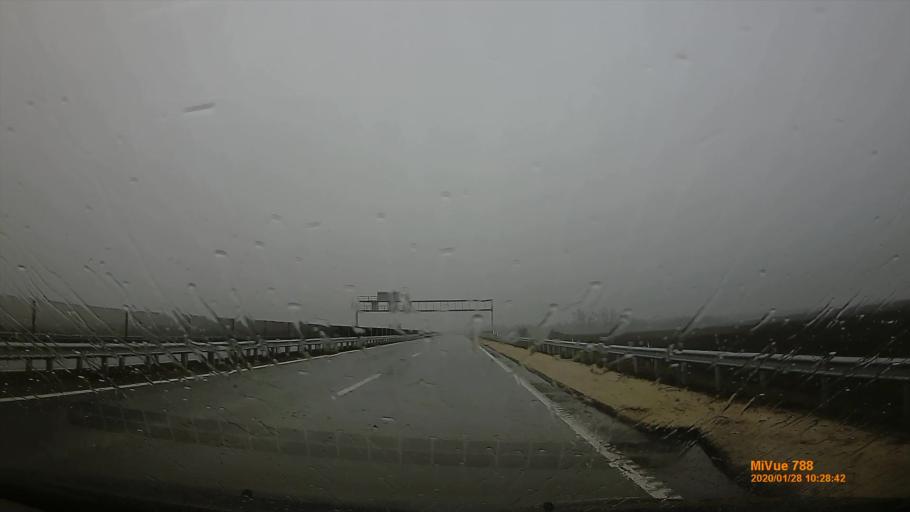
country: HU
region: Pest
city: Pilis
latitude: 47.3188
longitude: 19.5438
